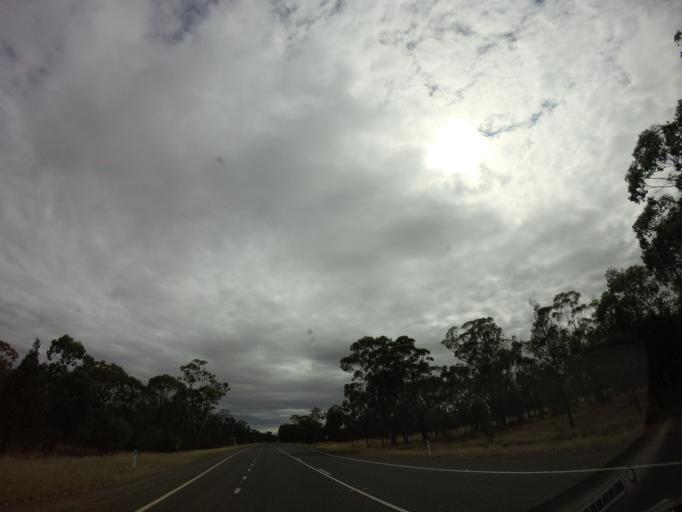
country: AU
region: New South Wales
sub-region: Narrabri
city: Narrabri
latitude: -30.3691
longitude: 149.7322
